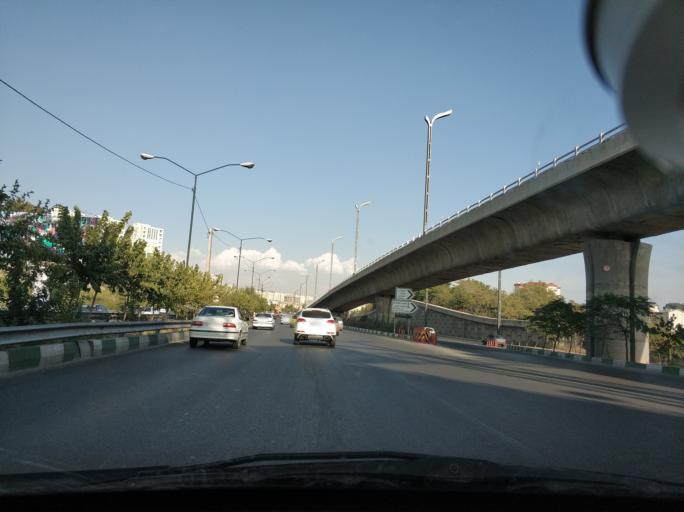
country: IR
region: Tehran
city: Tajrish
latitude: 35.7856
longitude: 51.4937
